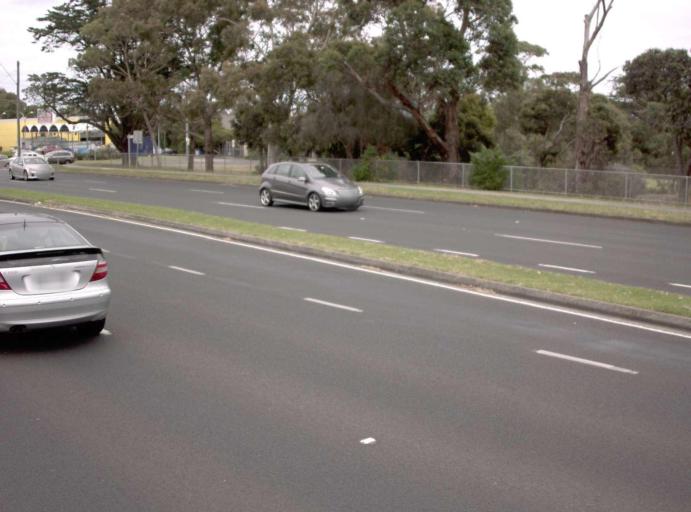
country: AU
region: Victoria
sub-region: Mornington Peninsula
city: Mornington
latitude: -38.2324
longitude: 145.0413
